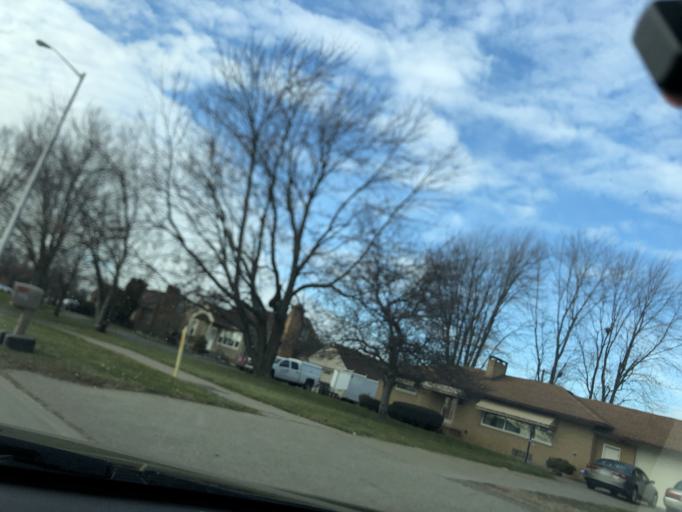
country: US
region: Michigan
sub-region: Wayne County
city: Taylor
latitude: 42.2121
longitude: -83.2658
